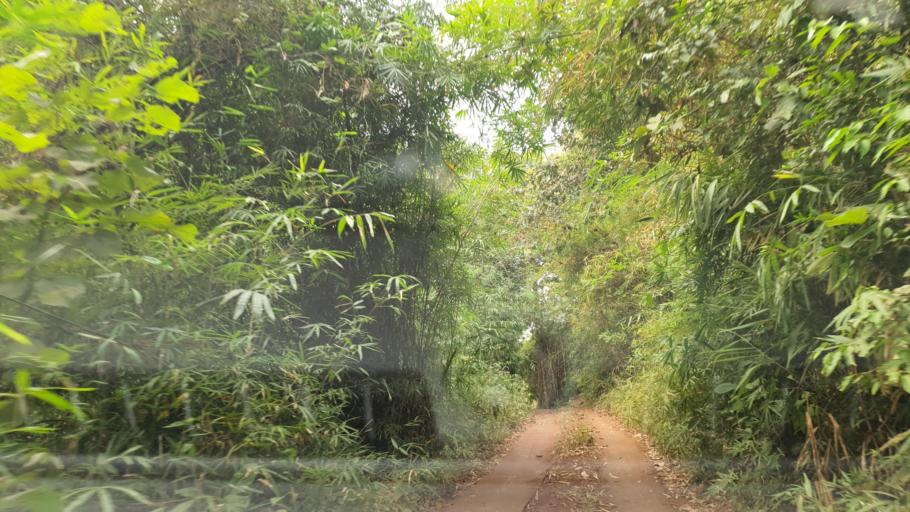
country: TH
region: Chiang Mai
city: Mae Wang
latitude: 18.6554
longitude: 98.6529
